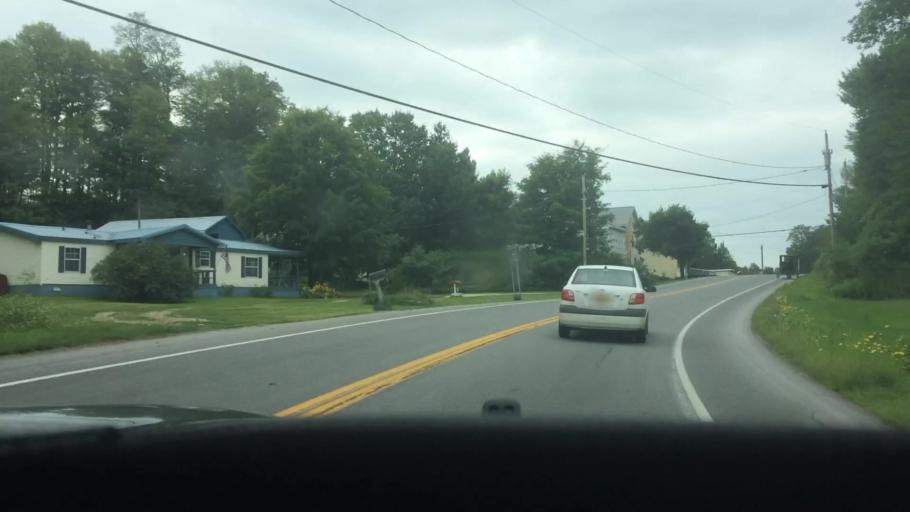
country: US
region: New York
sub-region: St. Lawrence County
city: Canton
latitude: 44.4999
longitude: -75.3426
